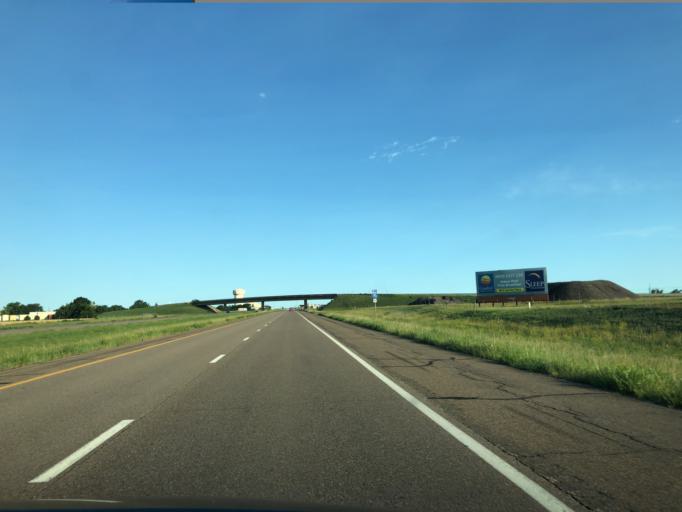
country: US
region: Kansas
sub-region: Ellis County
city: Hays
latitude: 38.8846
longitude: -99.2865
